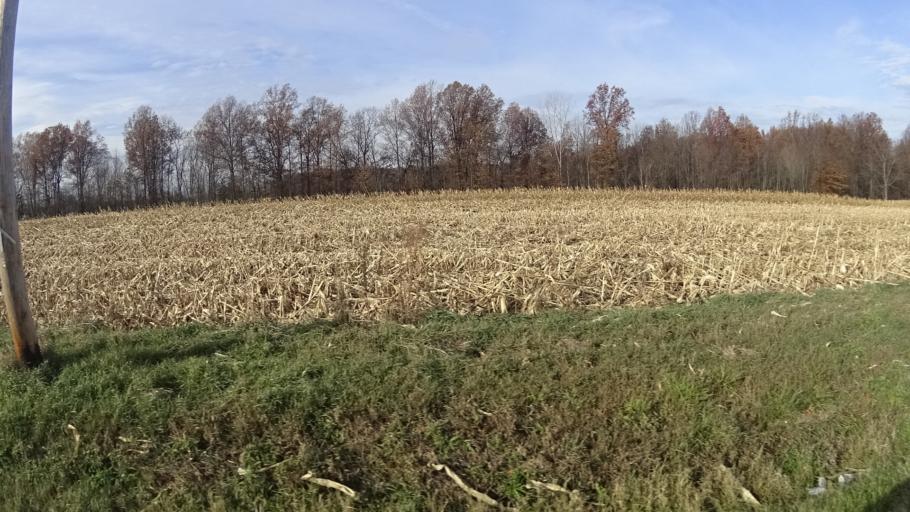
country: US
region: Ohio
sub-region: Lorain County
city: Grafton
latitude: 41.2273
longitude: -81.9835
